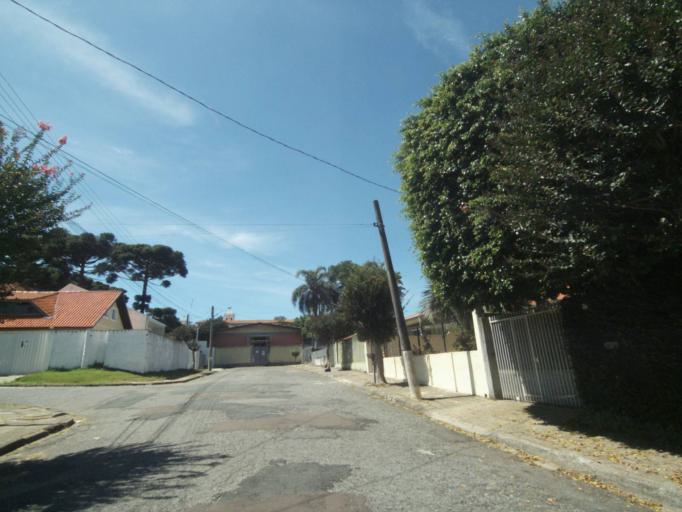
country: BR
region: Parana
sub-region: Curitiba
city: Curitiba
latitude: -25.4631
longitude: -49.2384
